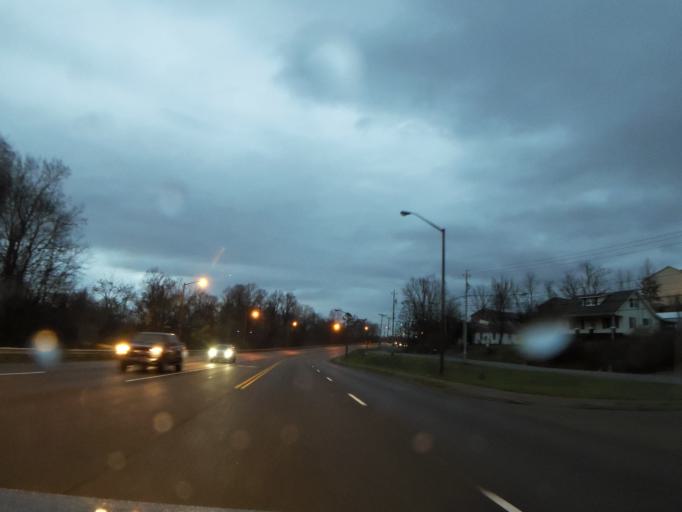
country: US
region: Tennessee
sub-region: Washington County
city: Midway
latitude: 36.3181
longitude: -82.3923
